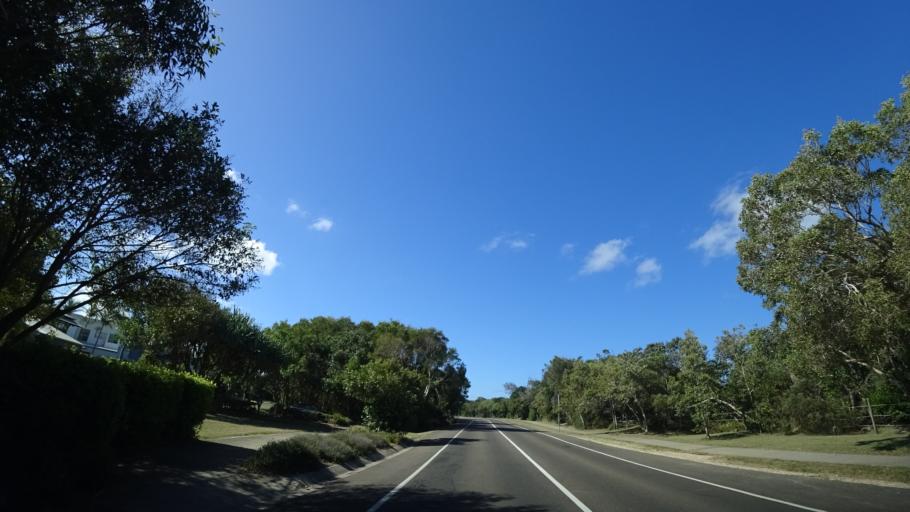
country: AU
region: Queensland
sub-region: Sunshine Coast
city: Mooloolaba
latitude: -26.6106
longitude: 153.0991
